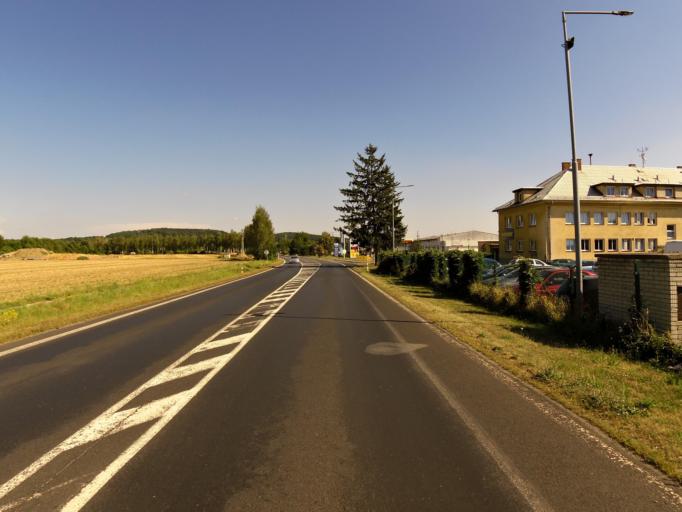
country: CZ
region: Central Bohemia
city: Mnichovo Hradiste
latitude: 50.5170
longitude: 14.9632
